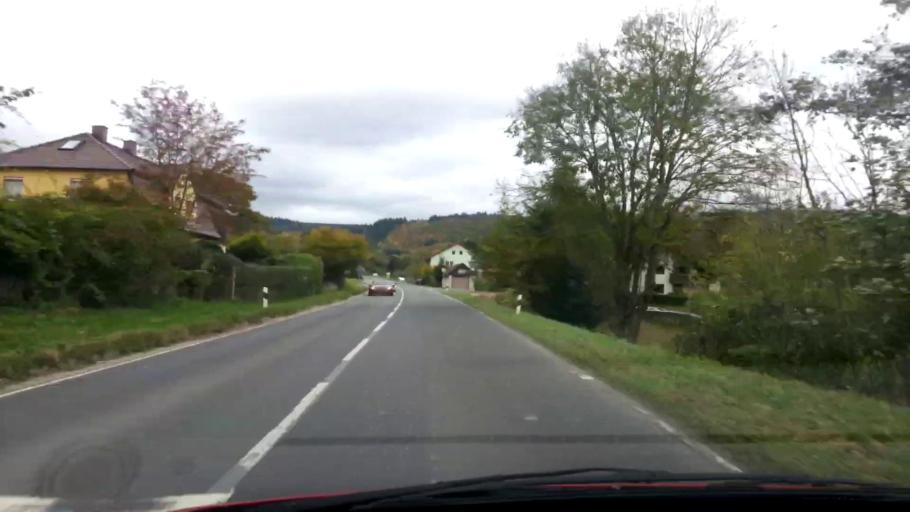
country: DE
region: Bavaria
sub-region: Upper Franconia
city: Kirchenpingarten
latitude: 49.9405
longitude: 11.7454
